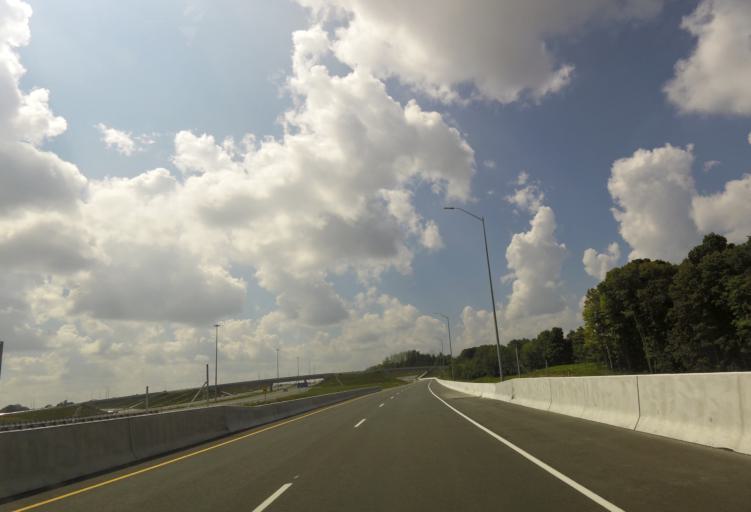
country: CA
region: Ontario
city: Ajax
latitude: 43.9517
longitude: -79.0008
